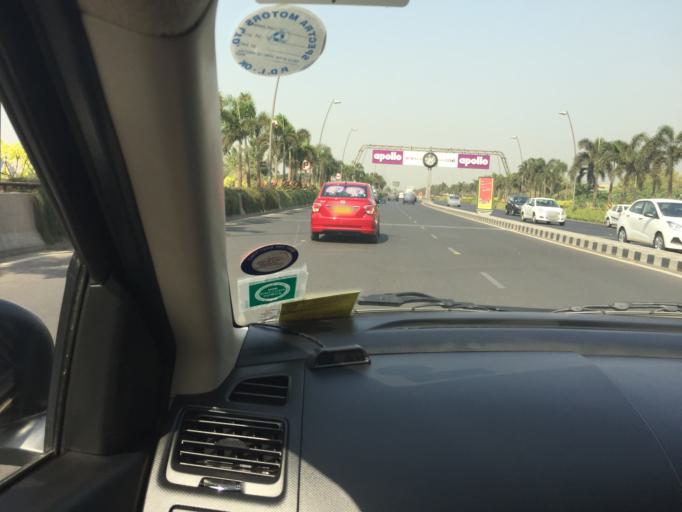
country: IN
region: Maharashtra
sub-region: Mumbai Suburban
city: Mumbai
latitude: 19.1029
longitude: 72.8688
